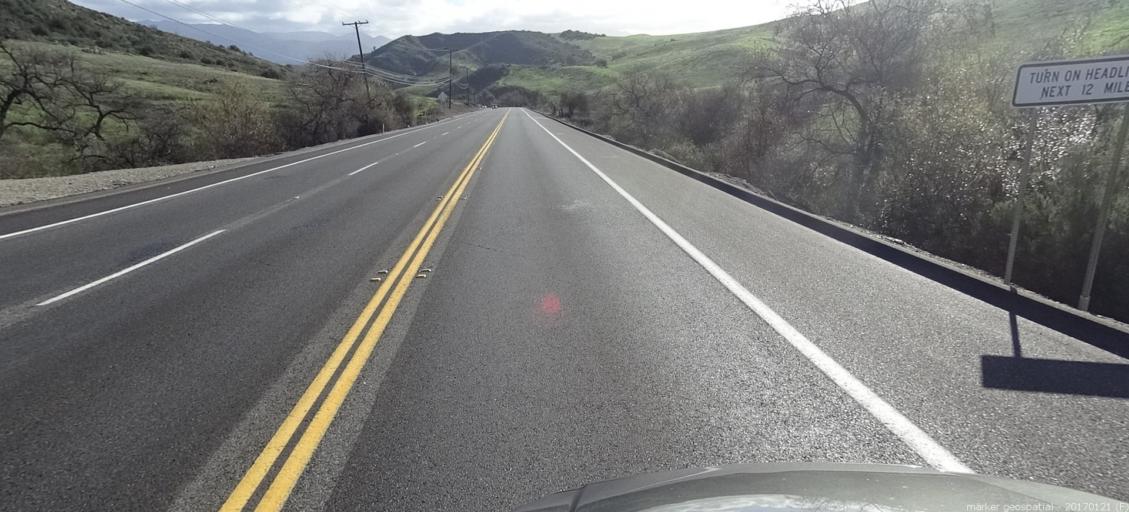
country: US
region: California
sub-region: Orange County
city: North Tustin
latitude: 33.7688
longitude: -117.7342
